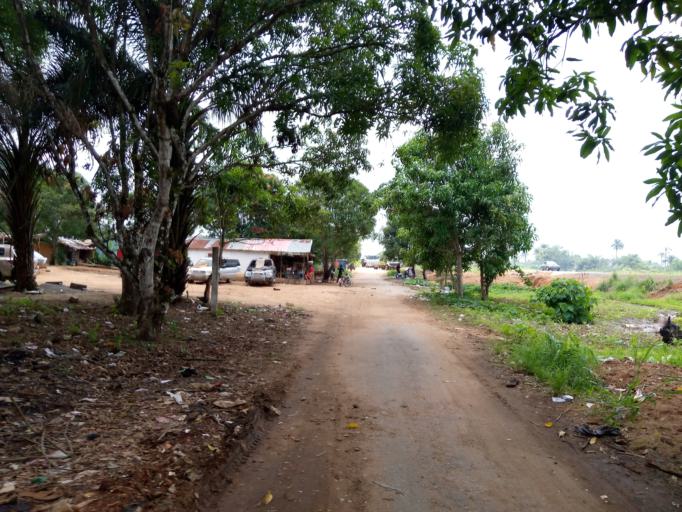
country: SL
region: Western Area
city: Waterloo
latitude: 8.3919
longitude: -12.9438
